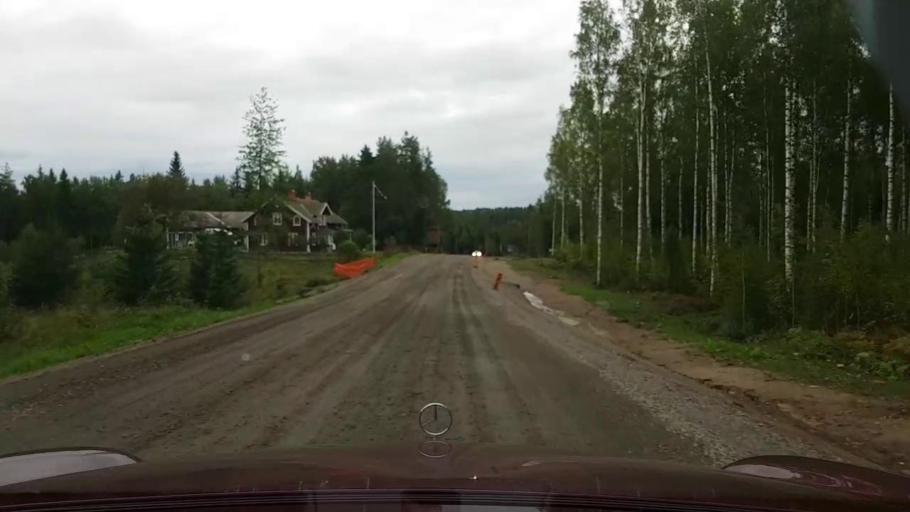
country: SE
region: Vaestra Goetaland
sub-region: Karlsborgs Kommun
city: Karlsborg
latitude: 58.7104
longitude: 14.5047
